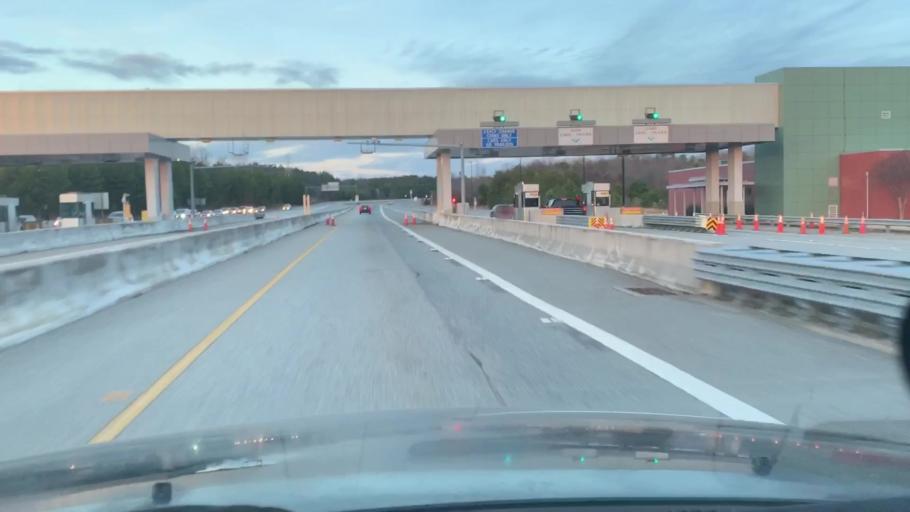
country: US
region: South Carolina
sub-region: Greenville County
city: Mauldin
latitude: 34.7435
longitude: -82.3155
